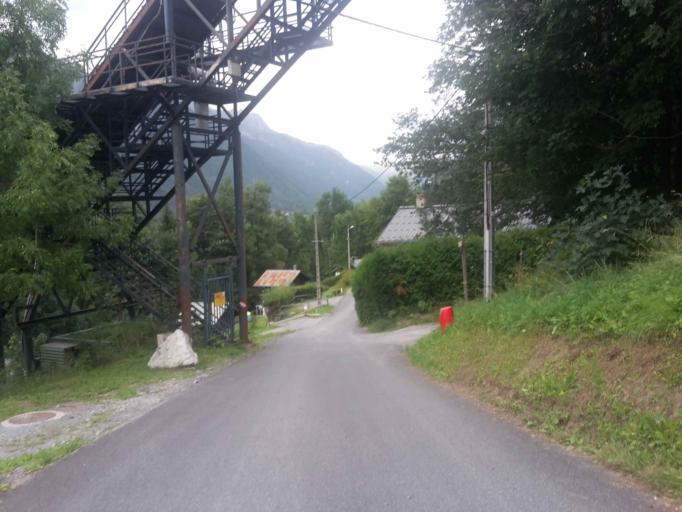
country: FR
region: Rhone-Alpes
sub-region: Departement de la Haute-Savoie
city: Chamonix-Mont-Blanc
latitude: 45.8973
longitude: 6.8427
